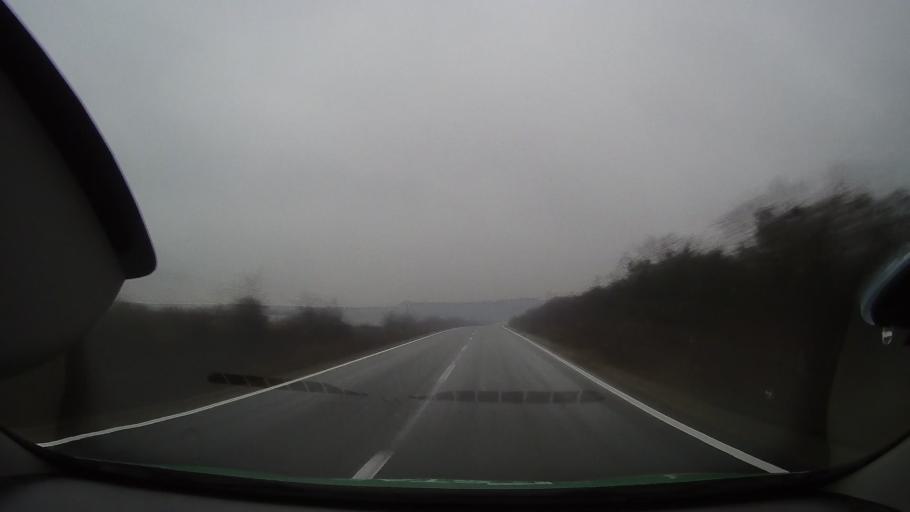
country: RO
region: Bihor
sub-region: Comuna Olcea
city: Olcea
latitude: 46.7081
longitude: 21.9610
